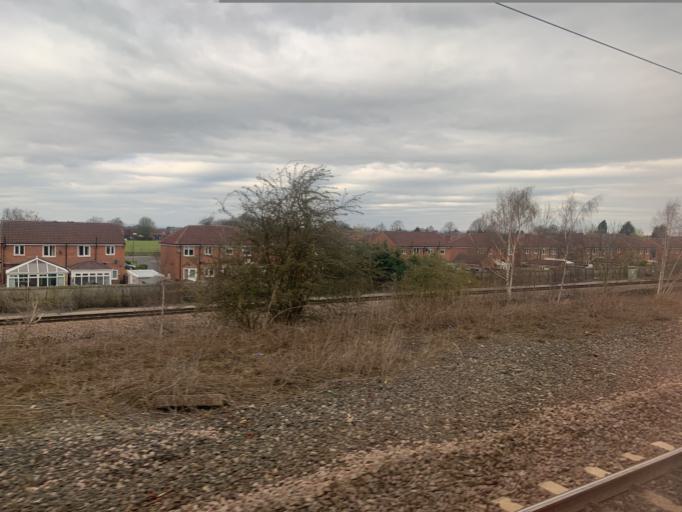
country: GB
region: England
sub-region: North Yorkshire
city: Northallerton
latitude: 54.3288
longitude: -1.4392
